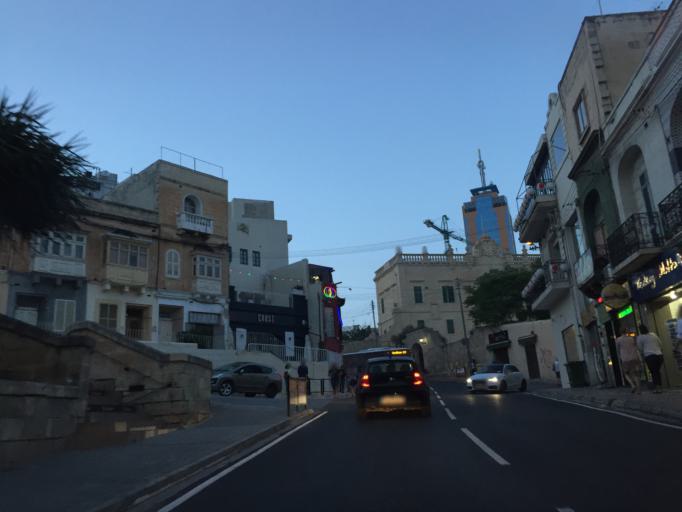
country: MT
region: Saint Julian
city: San Giljan
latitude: 35.9200
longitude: 14.4903
